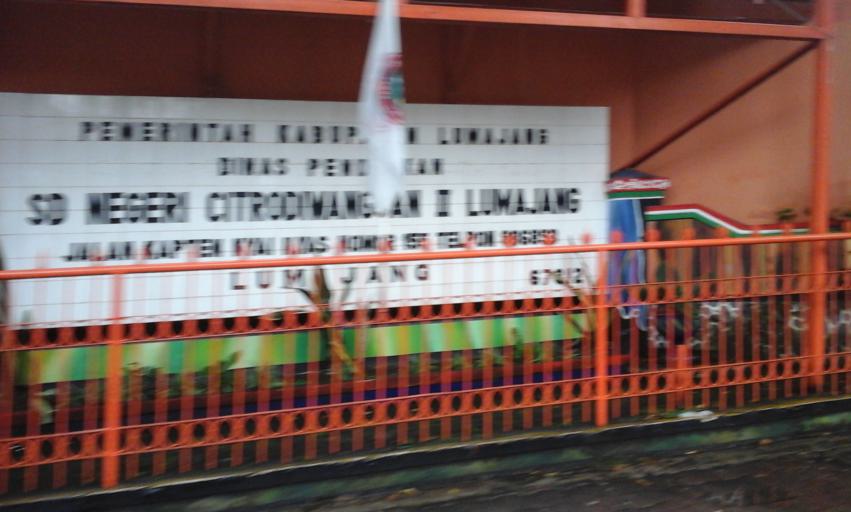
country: ID
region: East Java
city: Kadipaten
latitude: -8.1318
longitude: 113.2158
